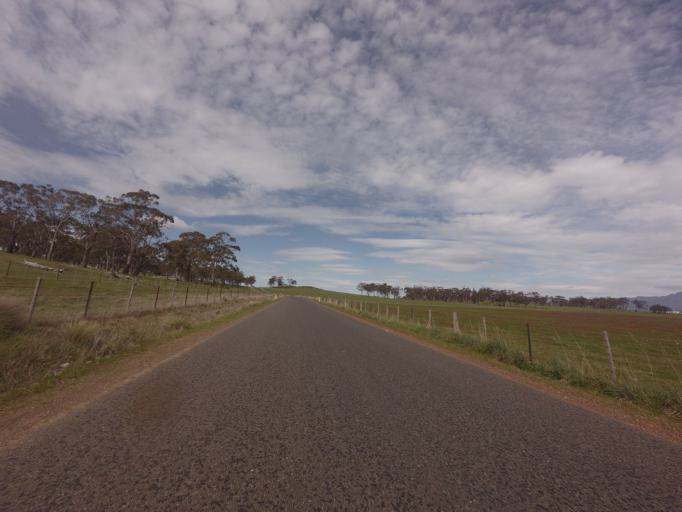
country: AU
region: Tasmania
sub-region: Northern Midlands
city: Longford
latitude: -41.7837
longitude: 147.2364
